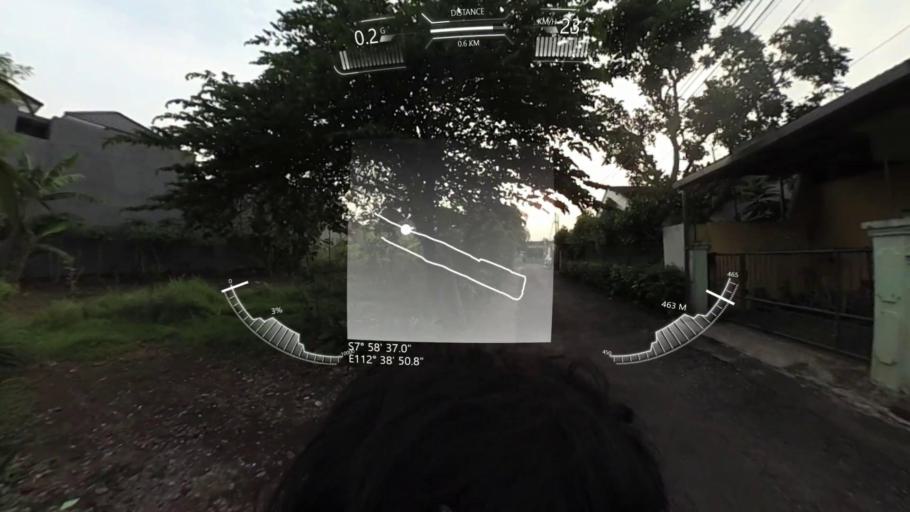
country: ID
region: East Java
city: Malang
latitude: -7.9770
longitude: 112.6475
